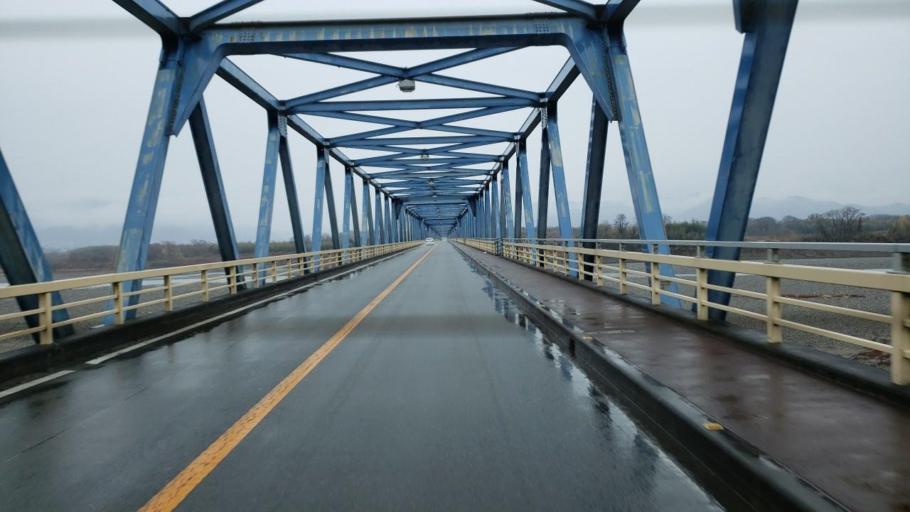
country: JP
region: Tokushima
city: Kamojimacho-jogejima
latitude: 34.0650
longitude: 134.2809
